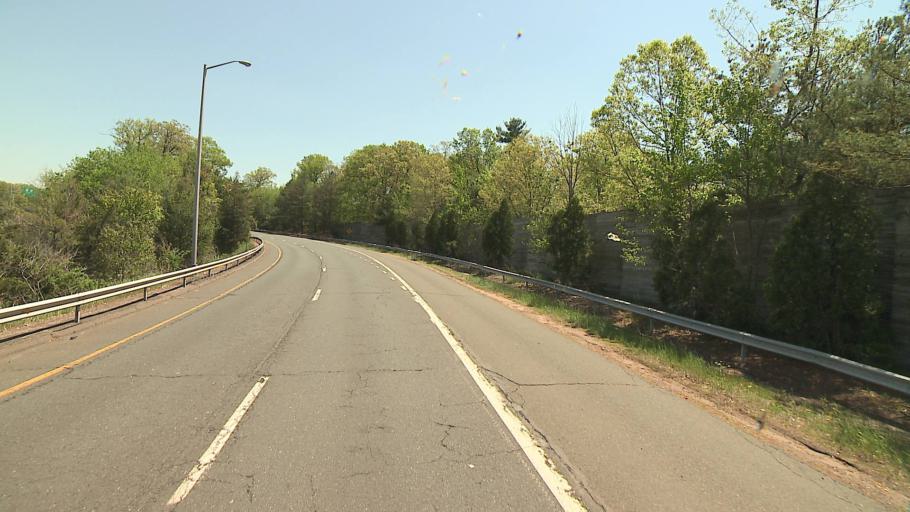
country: US
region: Connecticut
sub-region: Hartford County
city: Manchester
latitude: 41.8233
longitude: -72.4964
